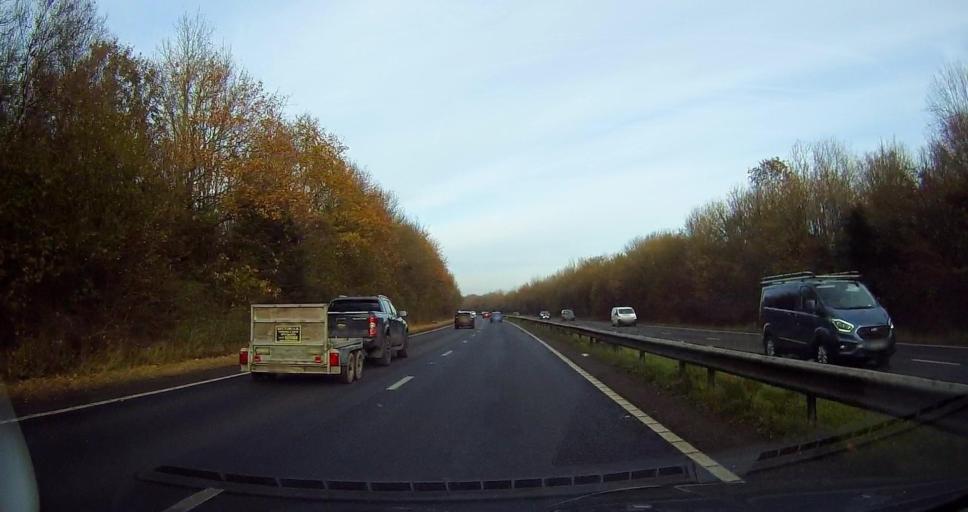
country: GB
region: England
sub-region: West Sussex
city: Hurstpierpoint
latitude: 50.9491
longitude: -0.1931
